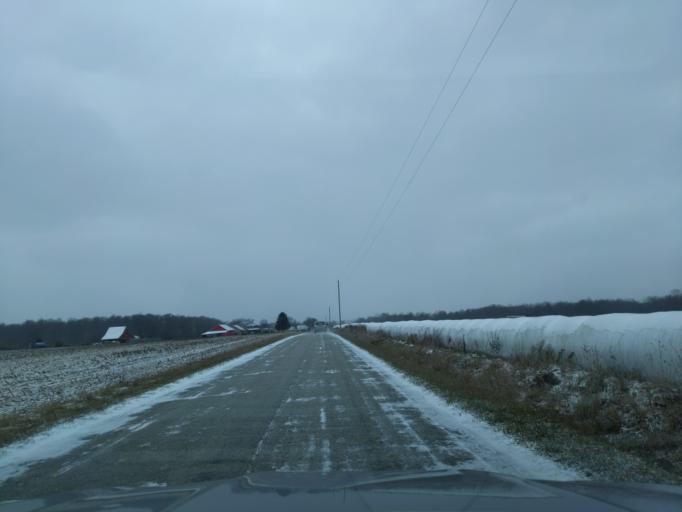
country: US
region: Indiana
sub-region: Decatur County
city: Westport
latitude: 39.2288
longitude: -85.4997
